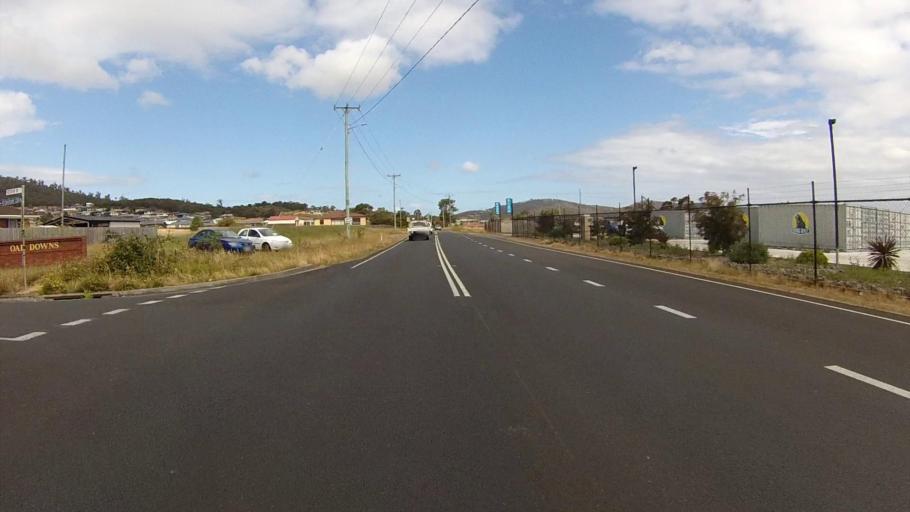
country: AU
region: Tasmania
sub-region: Clarence
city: Rokeby
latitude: -42.9029
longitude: 147.4499
